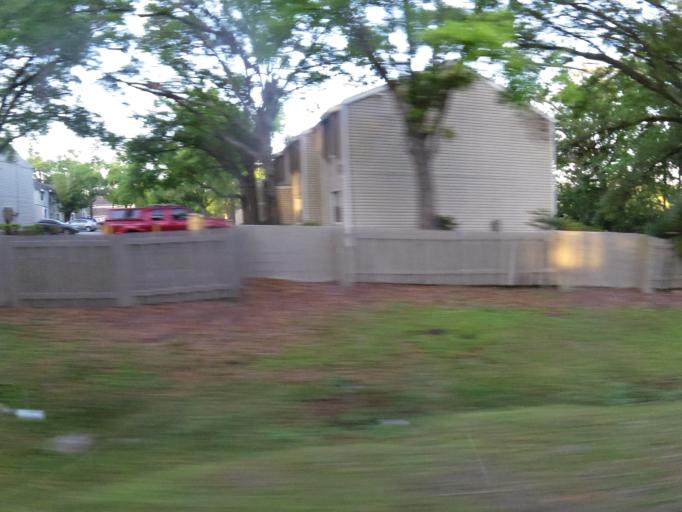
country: US
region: Florida
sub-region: Duval County
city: Jacksonville
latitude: 30.2820
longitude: -81.5726
